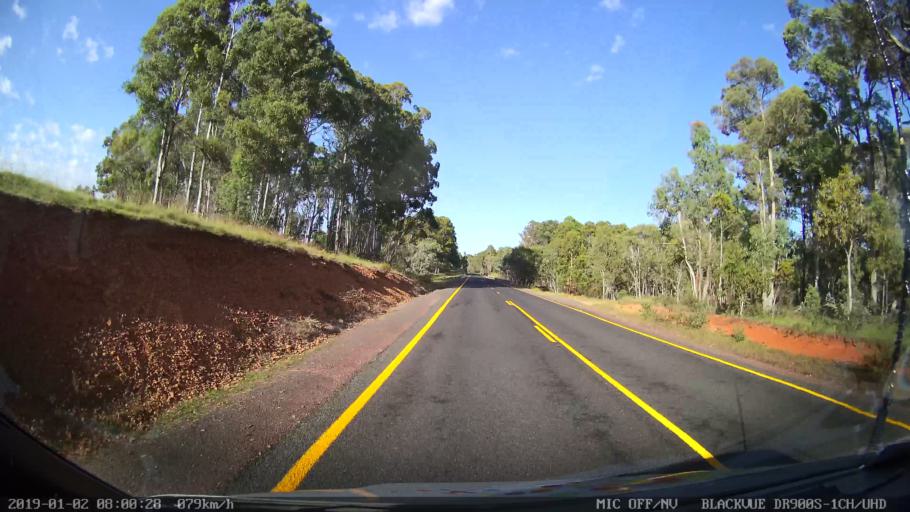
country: AU
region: New South Wales
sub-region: Tumut Shire
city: Tumut
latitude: -35.6445
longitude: 148.4450
